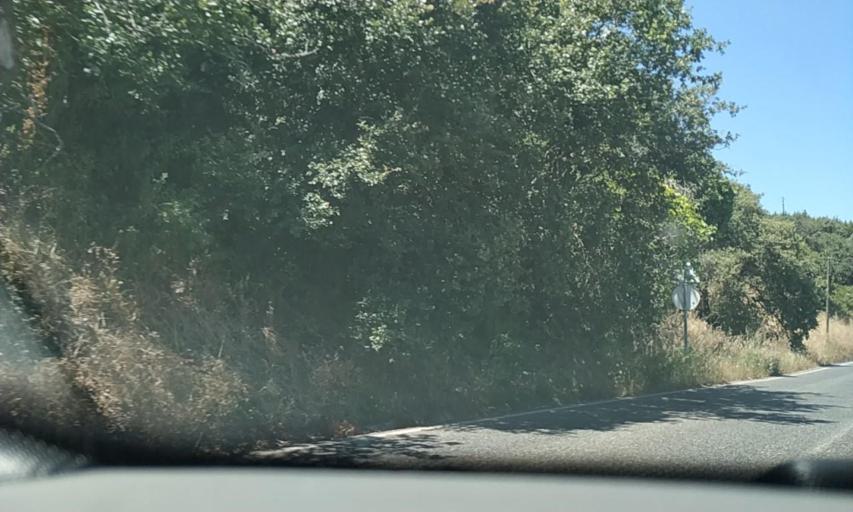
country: PT
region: Lisbon
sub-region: Odivelas
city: Canecas
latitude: 38.8579
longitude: -9.2101
